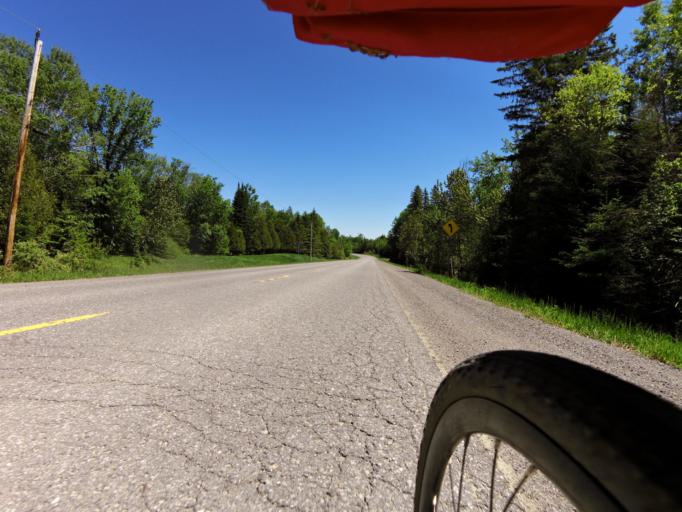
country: CA
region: Ontario
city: Carleton Place
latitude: 45.1838
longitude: -76.3894
